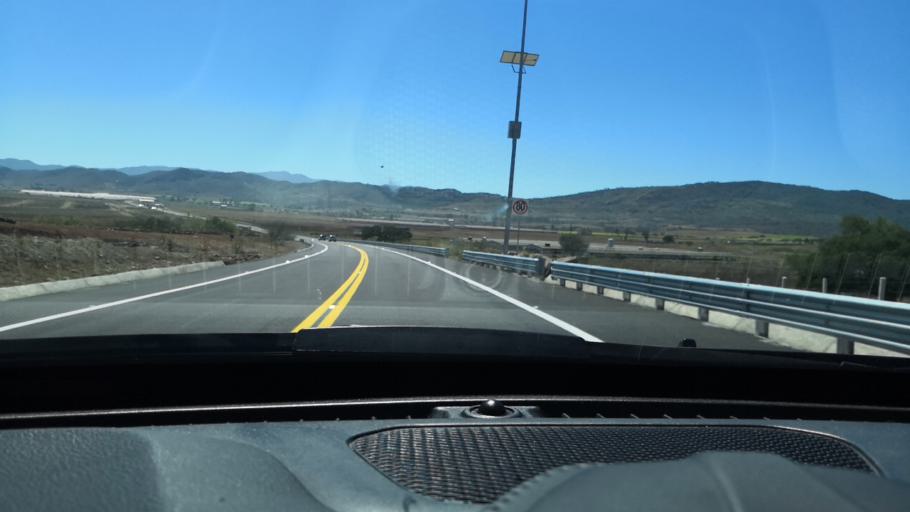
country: MX
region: Nayarit
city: Compostela
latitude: 21.2137
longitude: -104.8841
